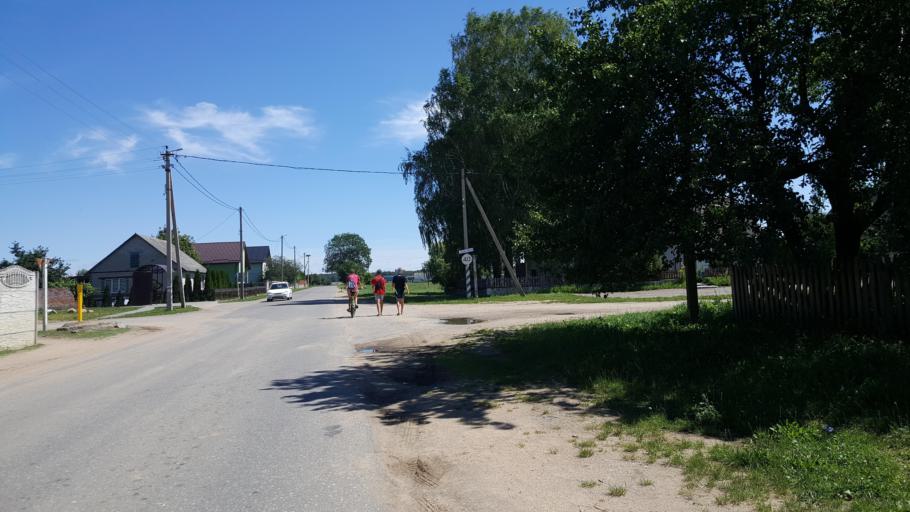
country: BY
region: Brest
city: Charnawchytsy
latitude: 52.2251
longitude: 23.7795
